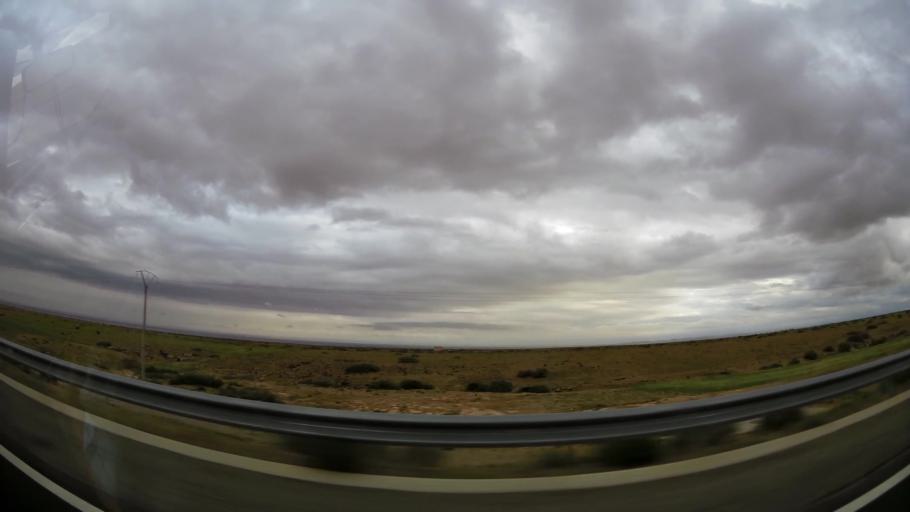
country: MA
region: Taza-Al Hoceima-Taounate
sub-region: Taza
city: Taza
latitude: 34.3073
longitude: -3.6900
